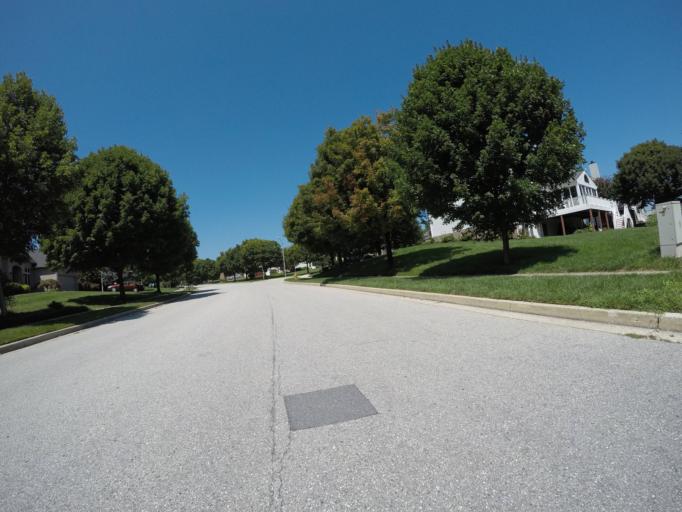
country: US
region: Maryland
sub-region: Howard County
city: Columbia
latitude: 39.2904
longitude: -76.8822
